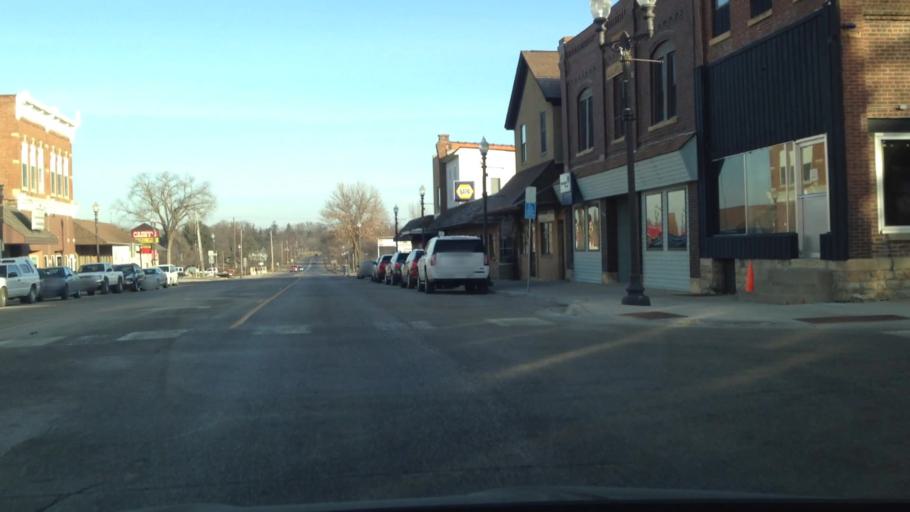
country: US
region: Minnesota
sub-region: Goodhue County
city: Zumbrota
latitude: 44.2941
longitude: -92.6691
